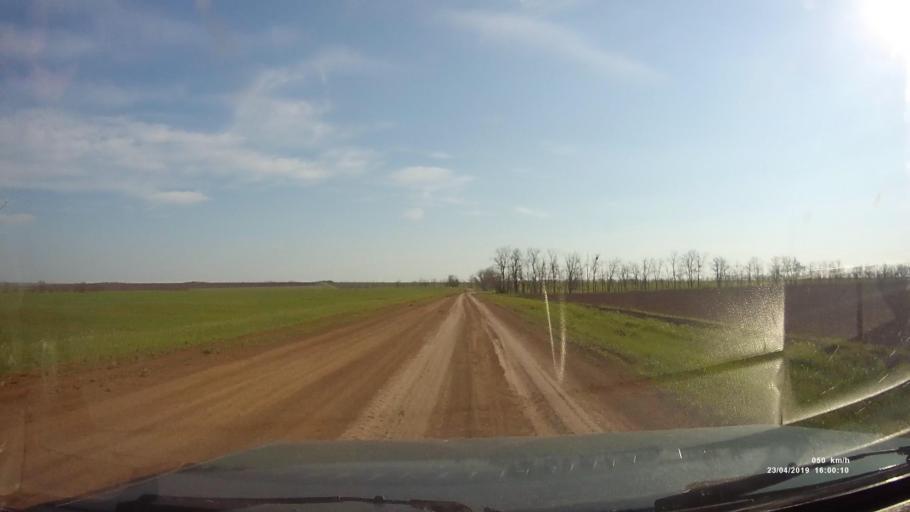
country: RU
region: Rostov
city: Remontnoye
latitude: 46.5112
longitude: 43.1083
